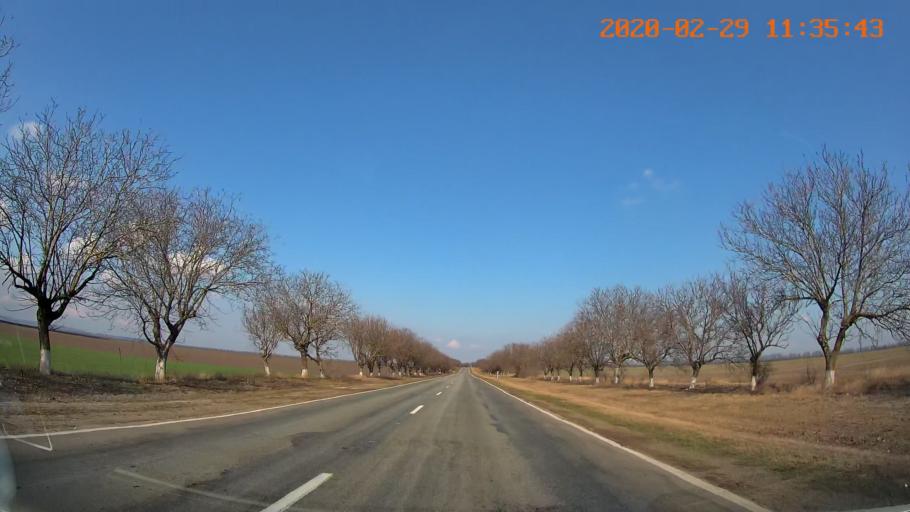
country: MD
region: Rezina
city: Saharna
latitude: 47.5848
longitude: 29.0615
